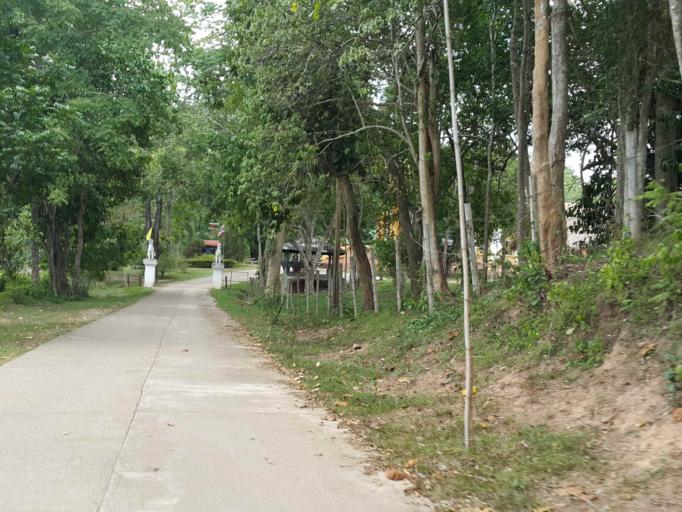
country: TH
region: Chiang Mai
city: Hang Dong
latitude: 18.7607
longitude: 98.9081
